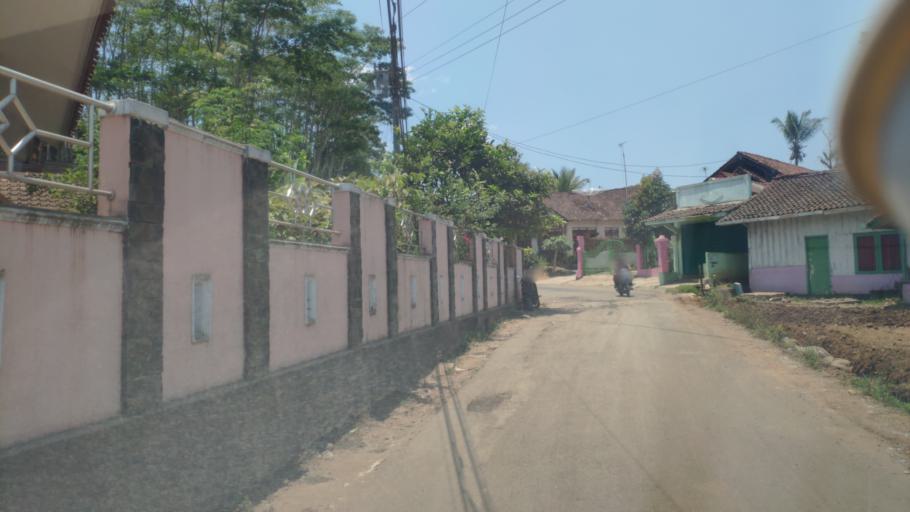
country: ID
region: Central Java
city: Wonosobo
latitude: -7.4002
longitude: 109.6960
